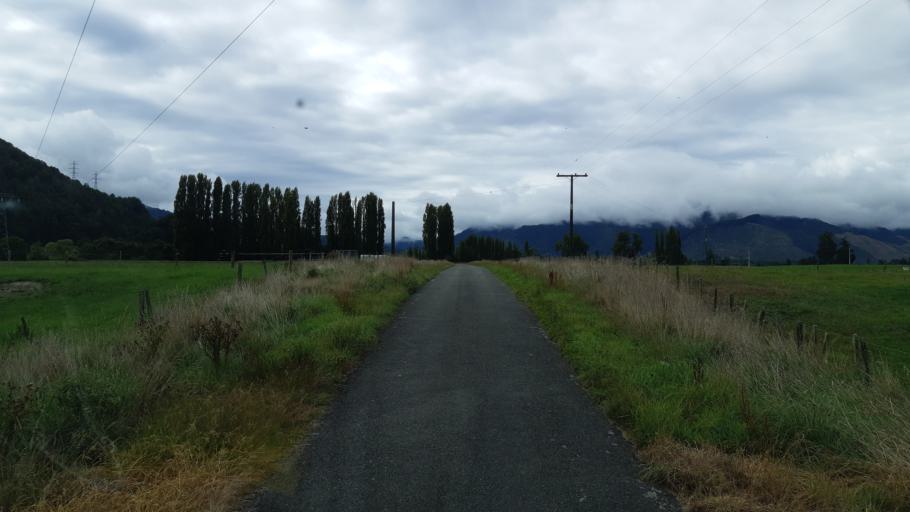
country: NZ
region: West Coast
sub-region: Buller District
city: Westport
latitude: -41.7766
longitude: 172.2919
